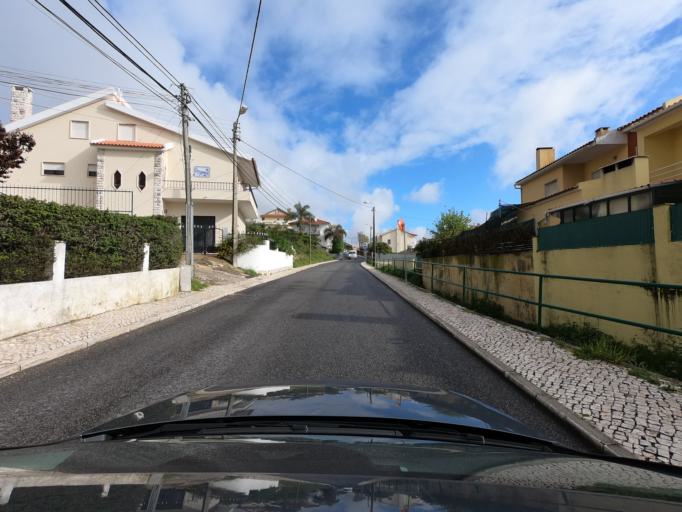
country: PT
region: Lisbon
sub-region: Oeiras
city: Porto Salvo
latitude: 38.7237
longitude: -9.3099
